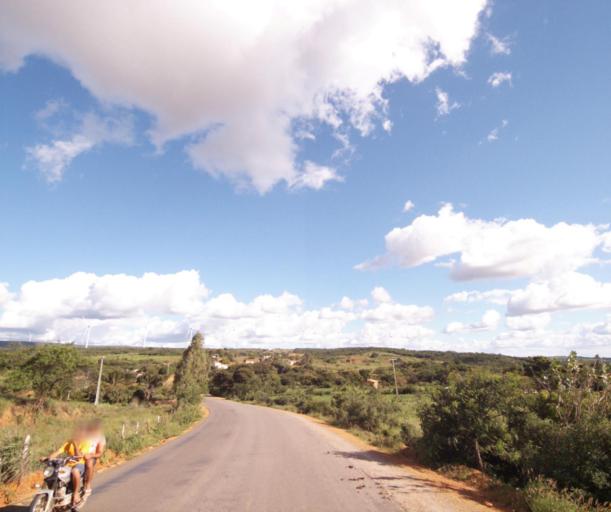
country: BR
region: Bahia
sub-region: Guanambi
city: Guanambi
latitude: -14.1450
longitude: -42.6444
